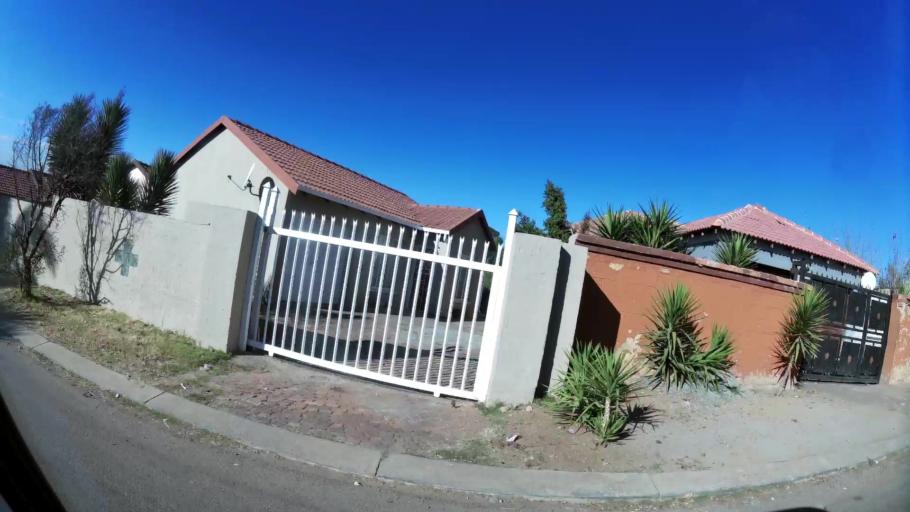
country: ZA
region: Gauteng
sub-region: City of Johannesburg Metropolitan Municipality
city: Midrand
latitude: -25.9063
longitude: 28.0974
